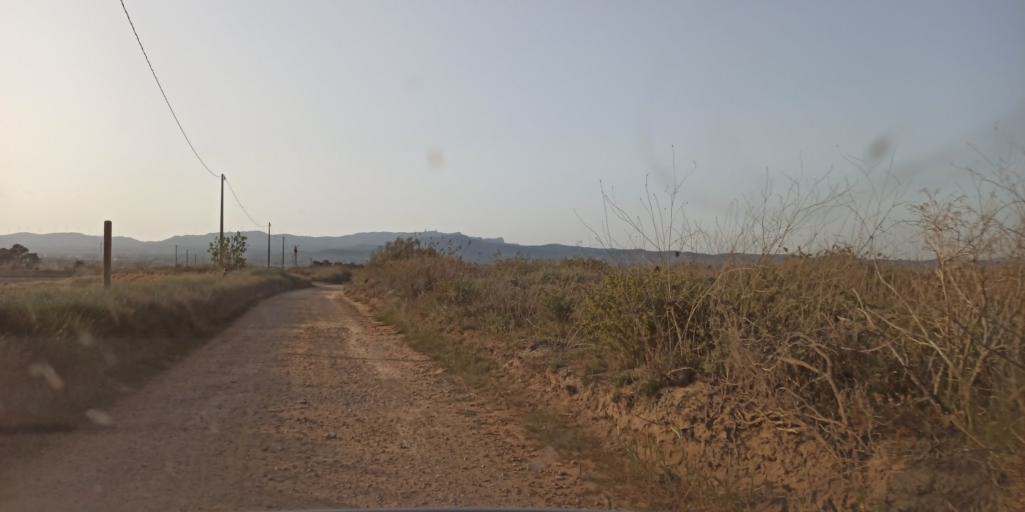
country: ES
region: Catalonia
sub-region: Provincia de Tarragona
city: L'Ampolla
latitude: 40.7830
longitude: 0.7128
